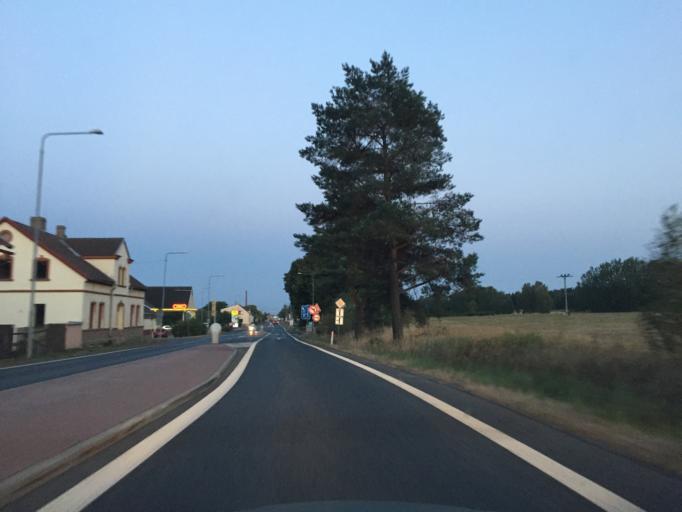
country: CZ
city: Cvikov
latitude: 50.7844
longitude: 14.6145
